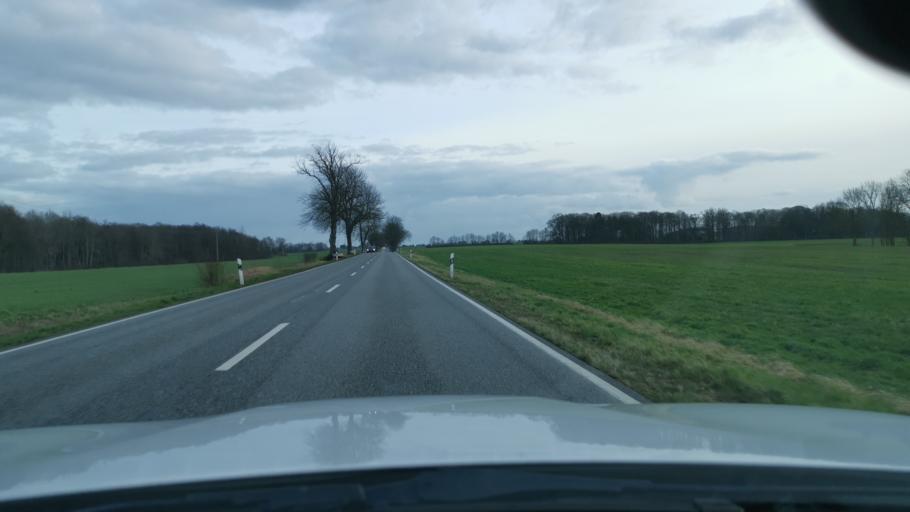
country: DE
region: Mecklenburg-Vorpommern
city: Dummerstorf
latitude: 53.9908
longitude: 12.2697
